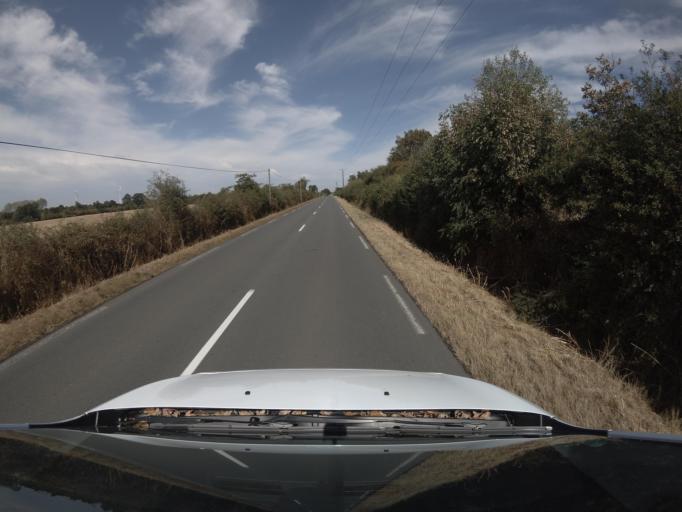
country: FR
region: Poitou-Charentes
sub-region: Departement des Deux-Sevres
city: Nueil-les-Aubiers
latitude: 46.9637
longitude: -0.5706
